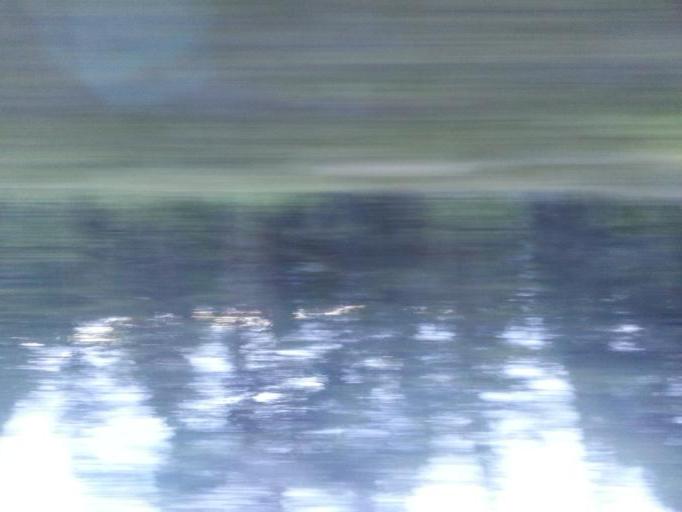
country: NO
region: Oppland
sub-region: Dovre
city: Dombas
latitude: 62.1107
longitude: 9.1075
